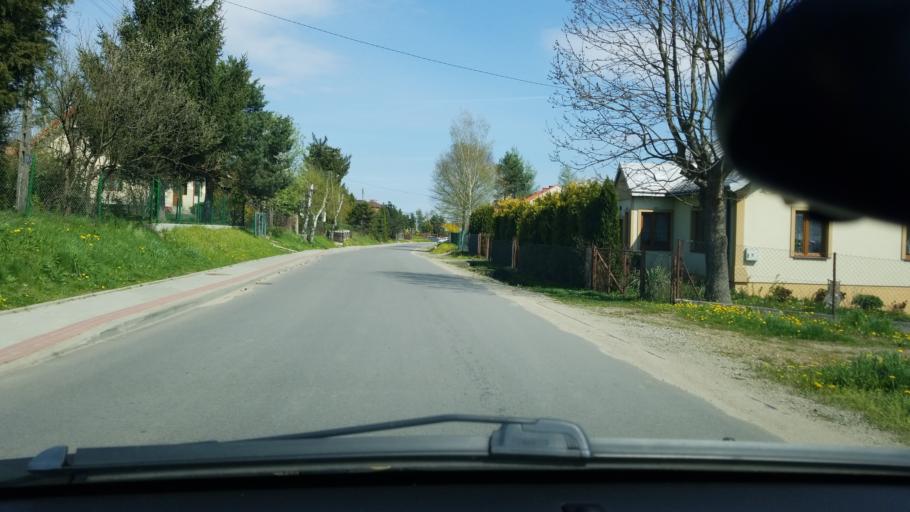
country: PL
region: Subcarpathian Voivodeship
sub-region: Powiat jasielski
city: Debowiec
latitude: 49.6858
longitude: 21.4651
